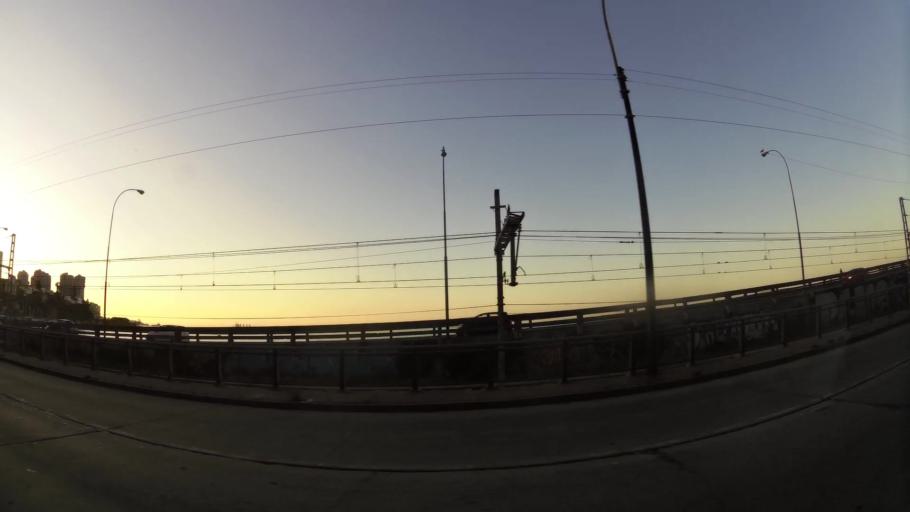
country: CL
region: Valparaiso
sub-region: Provincia de Valparaiso
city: Vina del Mar
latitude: -33.0263
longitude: -71.5739
